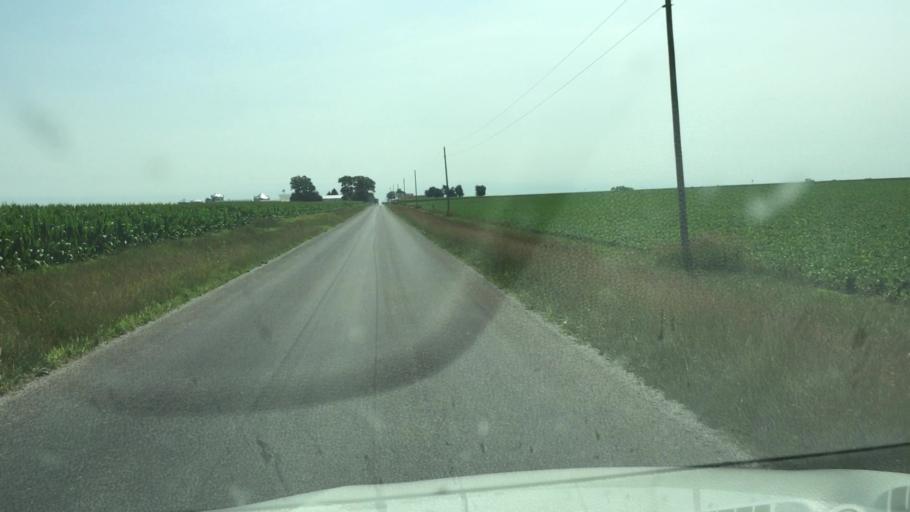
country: US
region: Illinois
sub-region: Hancock County
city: Nauvoo
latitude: 40.5074
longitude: -91.3209
